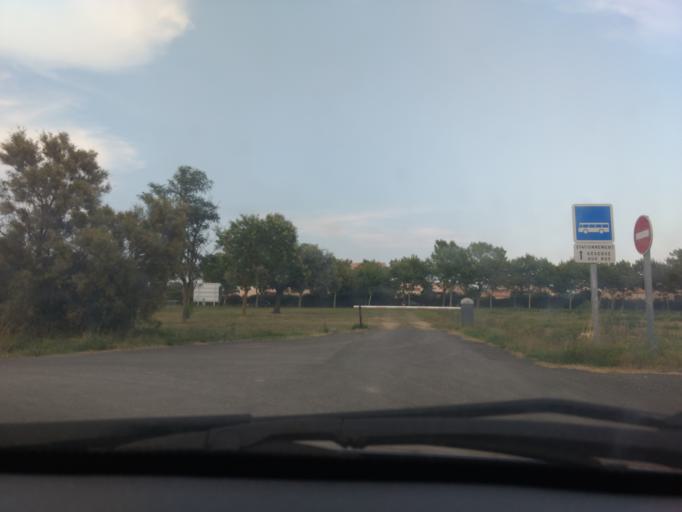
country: FR
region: Languedoc-Roussillon
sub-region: Departement des Pyrenees-Orientales
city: Latour-Bas-Elne
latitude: 42.6006
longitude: 3.0313
